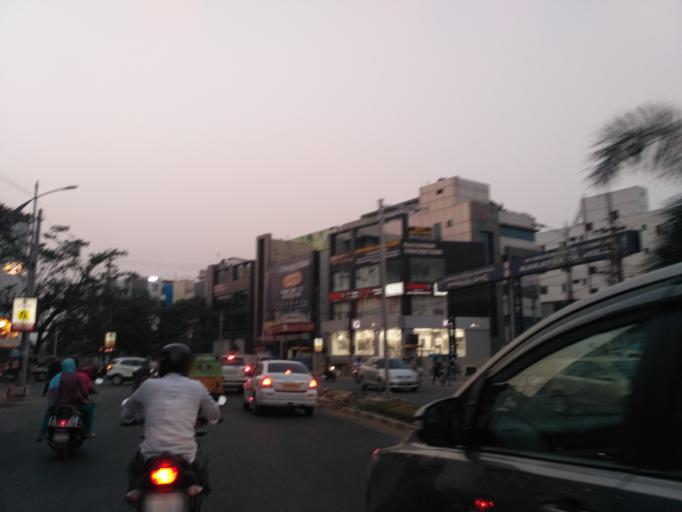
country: IN
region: Telangana
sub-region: Rangareddi
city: Kukatpalli
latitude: 17.4413
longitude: 78.3973
